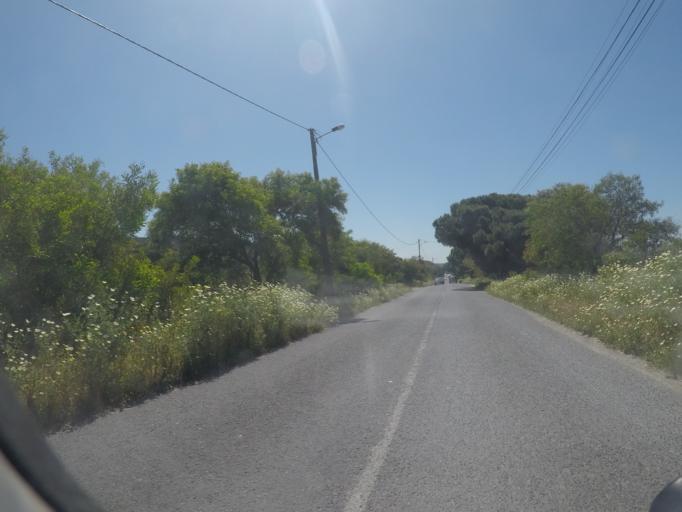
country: PT
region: Setubal
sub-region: Almada
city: Charneca
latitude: 38.6223
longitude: -9.2150
